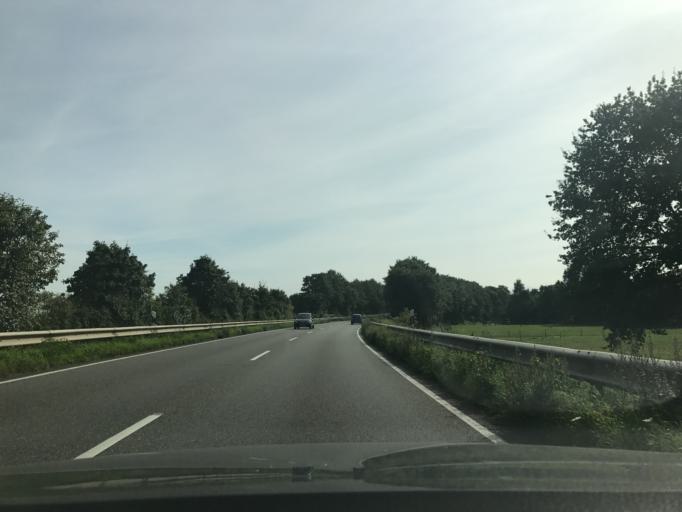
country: DE
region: North Rhine-Westphalia
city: Kempen
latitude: 51.3915
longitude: 6.4208
